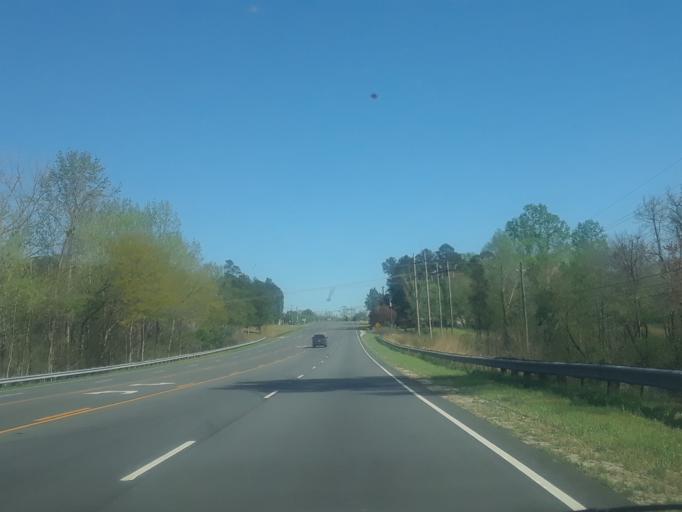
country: US
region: North Carolina
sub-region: Harnett County
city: Buies Creek
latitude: 35.3828
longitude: -78.7193
